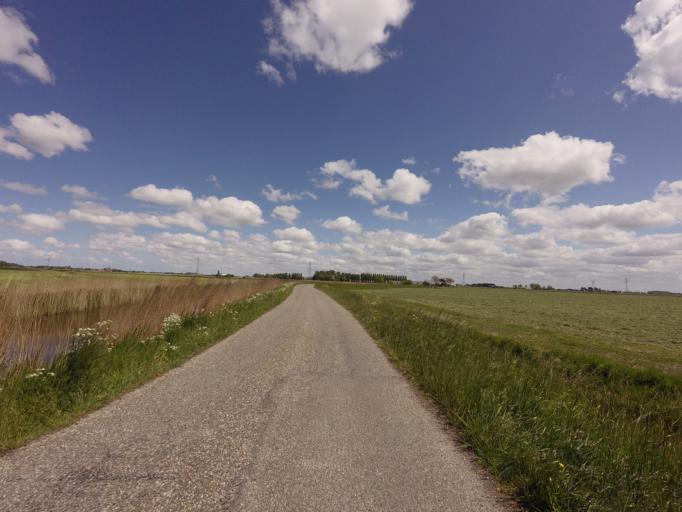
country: NL
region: Friesland
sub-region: Gemeente Franekeradeel
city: Franeker
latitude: 53.1473
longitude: 5.4922
